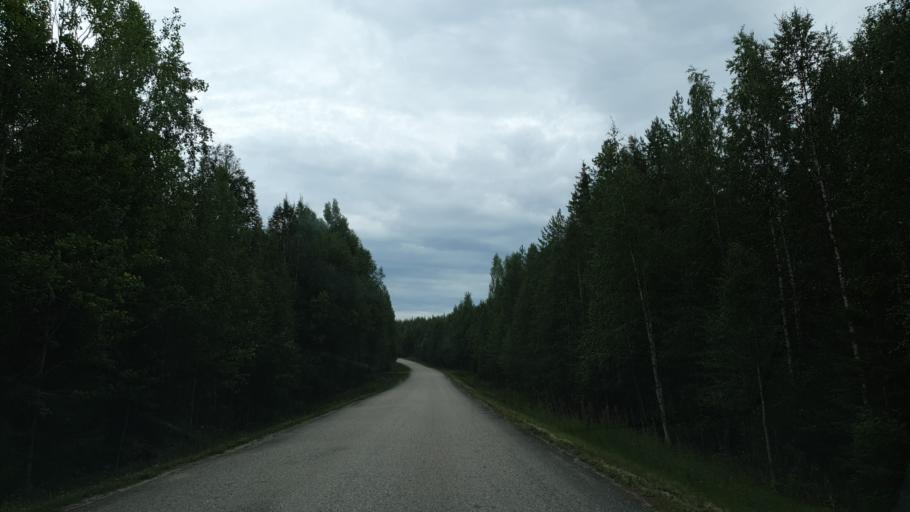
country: FI
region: Kainuu
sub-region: Kehys-Kainuu
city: Kuhmo
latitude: 64.3526
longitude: 29.0840
